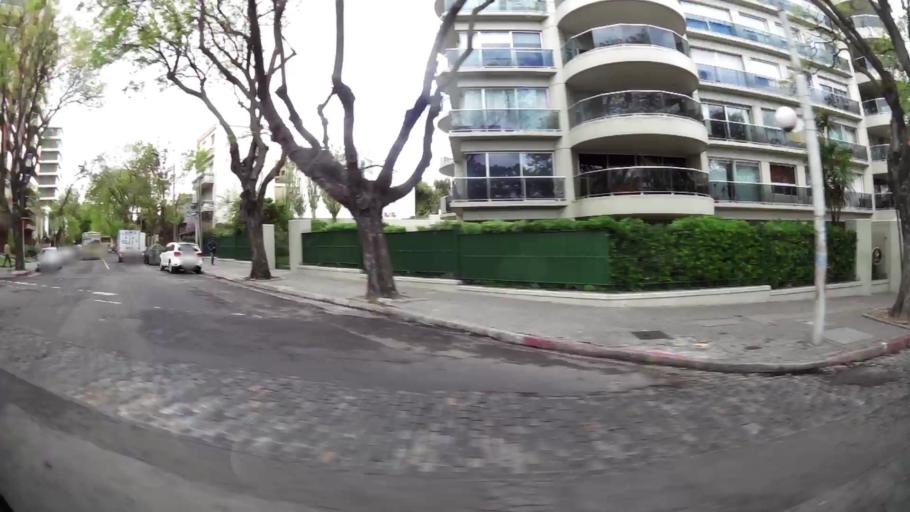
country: UY
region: Montevideo
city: Montevideo
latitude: -34.9255
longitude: -56.1615
